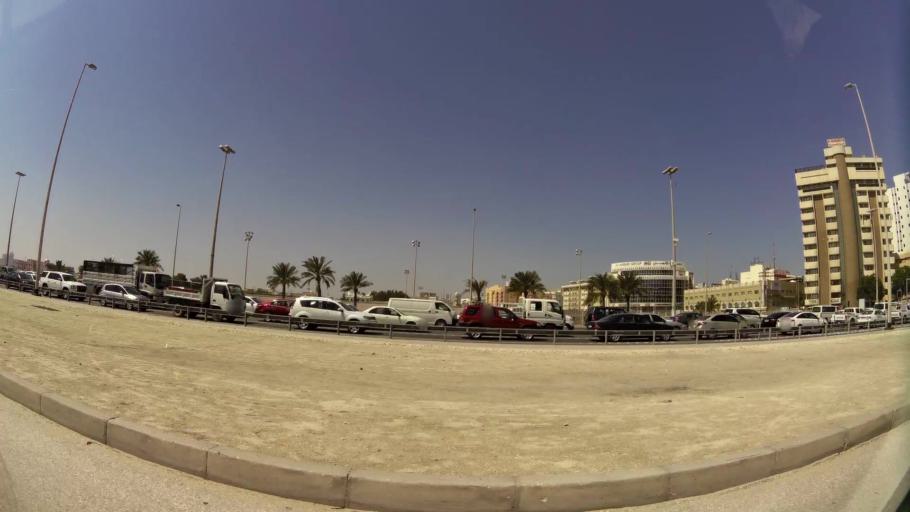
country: BH
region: Manama
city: Manama
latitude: 26.2233
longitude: 50.5981
